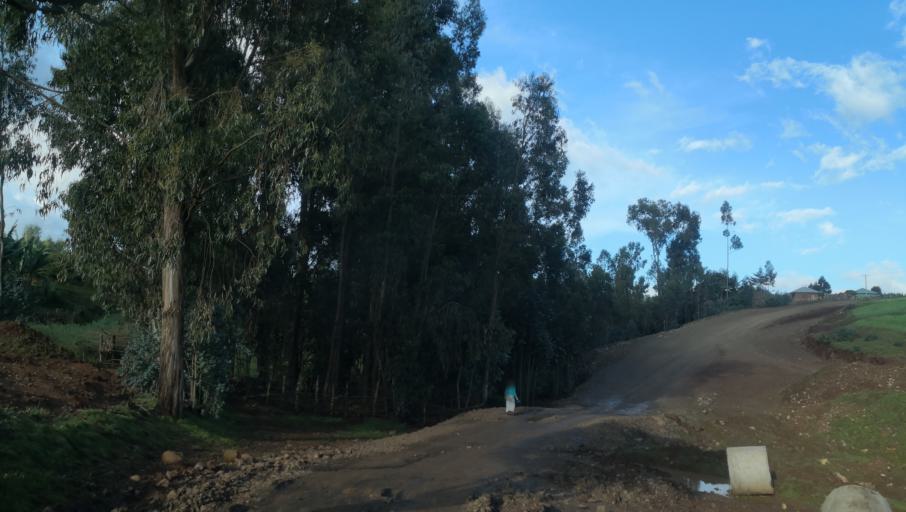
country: ET
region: Southern Nations, Nationalities, and People's Region
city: Butajira
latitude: 8.3919
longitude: 38.2957
